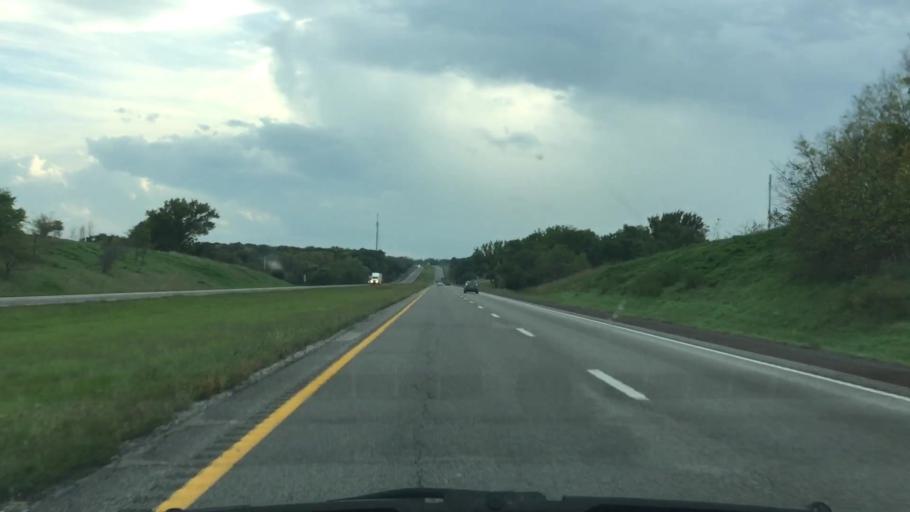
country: US
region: Missouri
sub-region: Clinton County
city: Cameron
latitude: 39.8836
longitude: -94.1609
